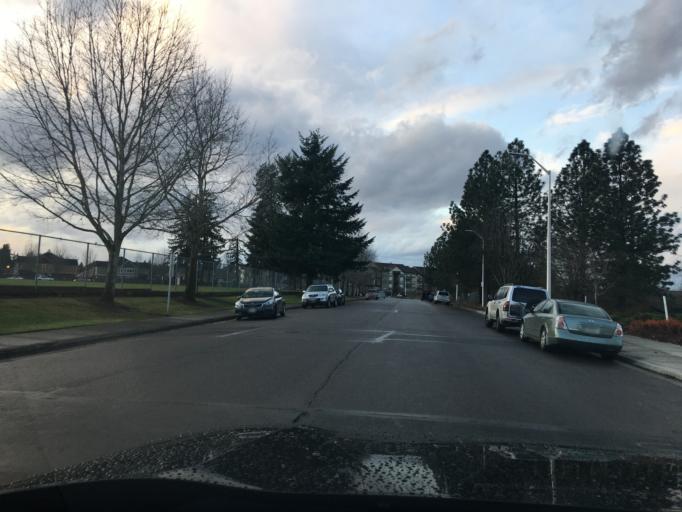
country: US
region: Oregon
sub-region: Washington County
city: Aloha
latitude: 45.5076
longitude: -122.8495
